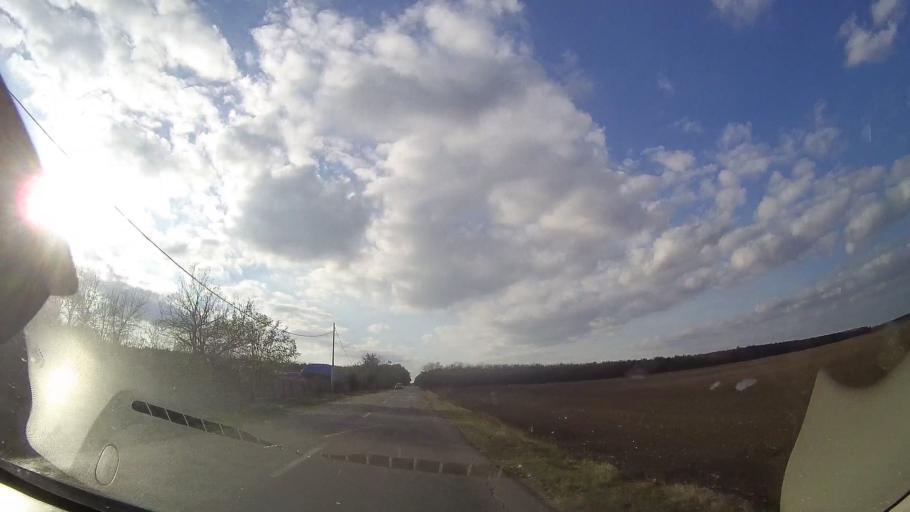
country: RO
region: Constanta
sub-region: Comuna Comana
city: Comana
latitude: 43.8193
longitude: 28.2870
